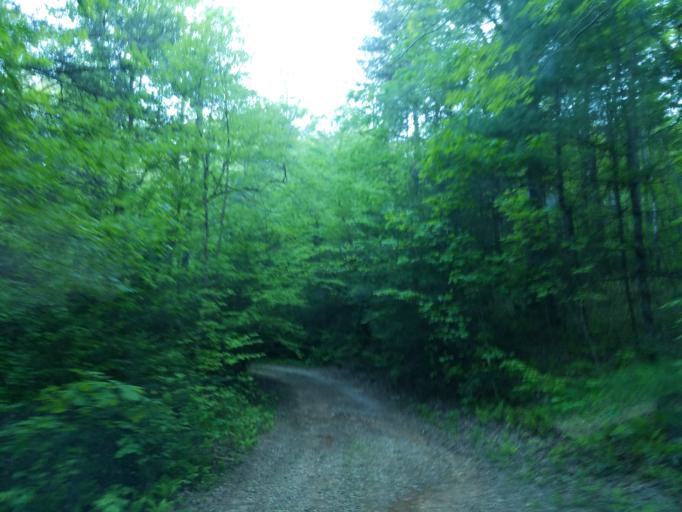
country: US
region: Georgia
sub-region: Lumpkin County
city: Dahlonega
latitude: 34.6672
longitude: -84.1313
